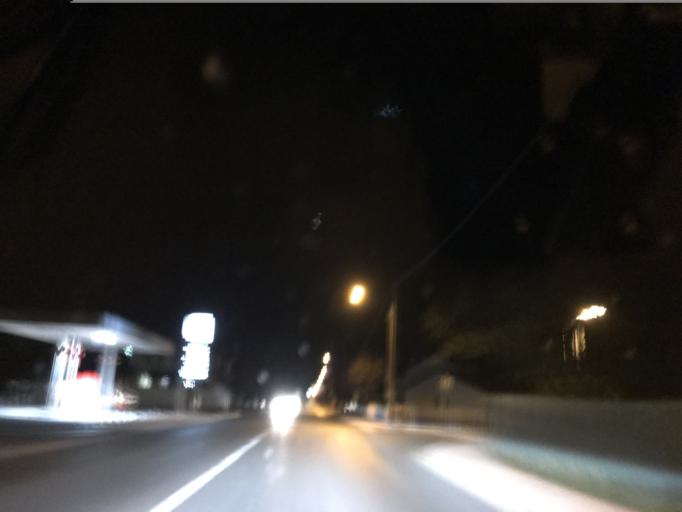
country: FR
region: Auvergne
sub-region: Departement du Puy-de-Dome
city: Puy-Guillaume
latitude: 45.9560
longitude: 3.4767
